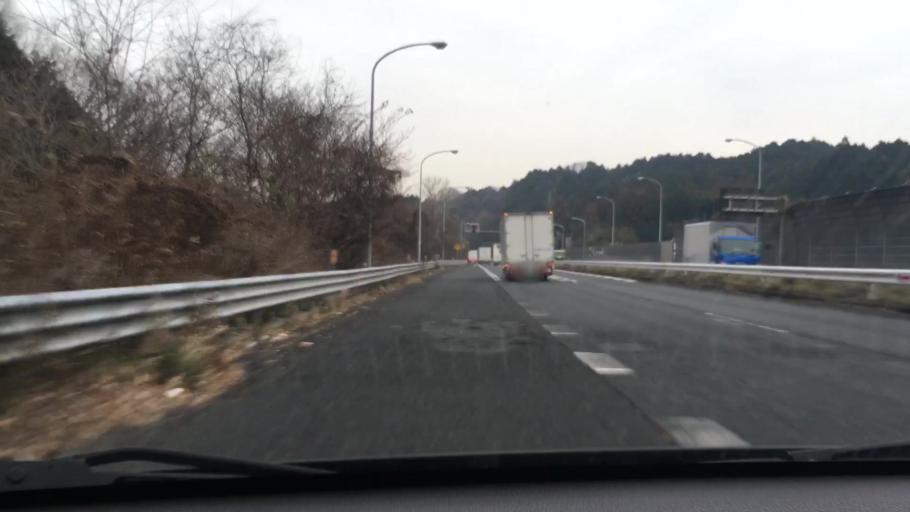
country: JP
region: Mie
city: Nabari
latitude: 34.6819
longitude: 136.0413
